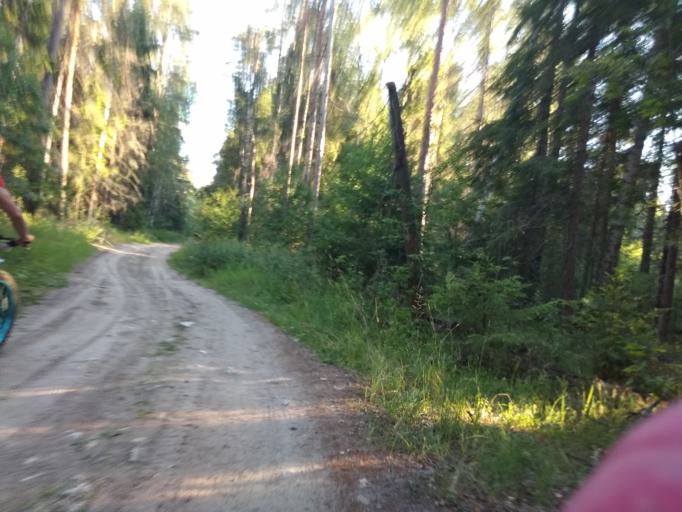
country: RU
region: Moskovskaya
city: Misheronskiy
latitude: 55.7352
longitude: 39.7695
